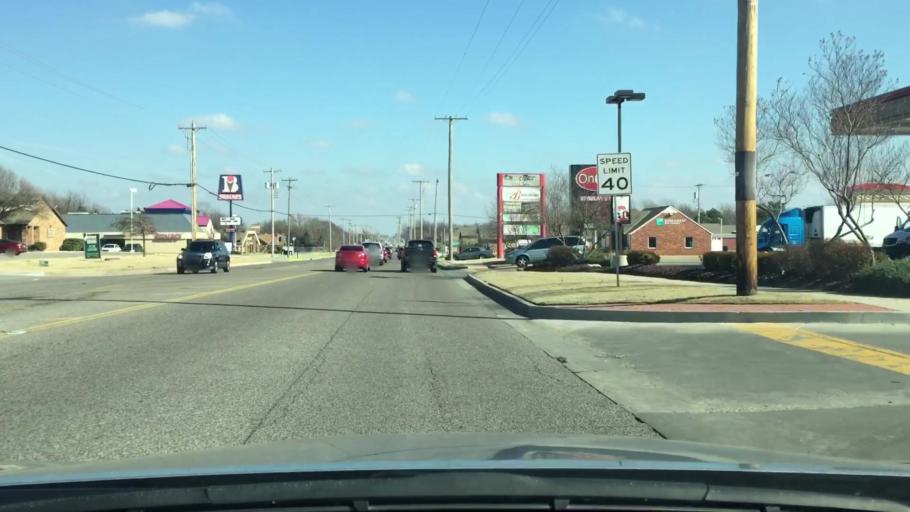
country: US
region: Oklahoma
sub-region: Cleveland County
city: Moore
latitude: 35.3771
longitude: -97.5471
